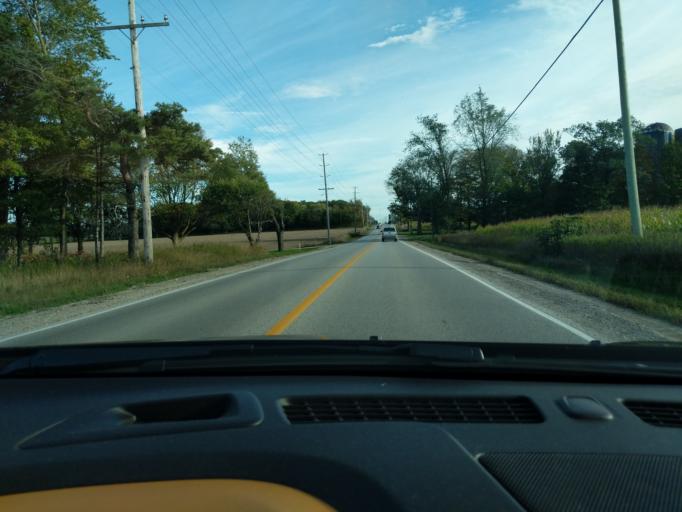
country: CA
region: Ontario
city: Barrie
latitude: 44.4044
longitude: -79.7447
